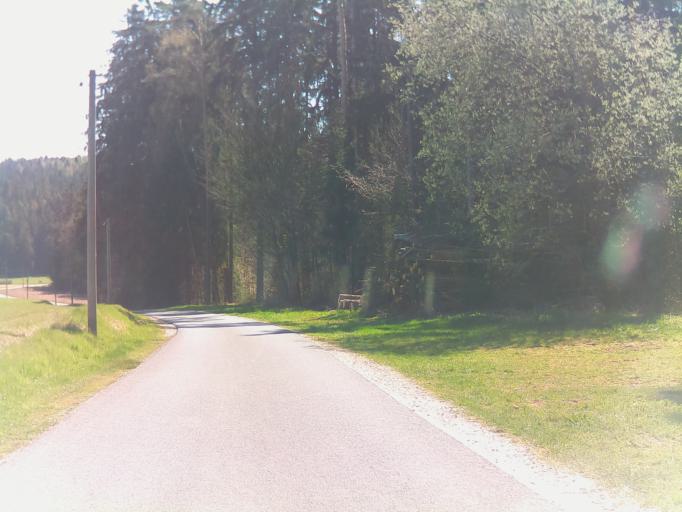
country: DE
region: Bavaria
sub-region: Upper Palatinate
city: Kastl
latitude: 49.3977
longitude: 11.6745
